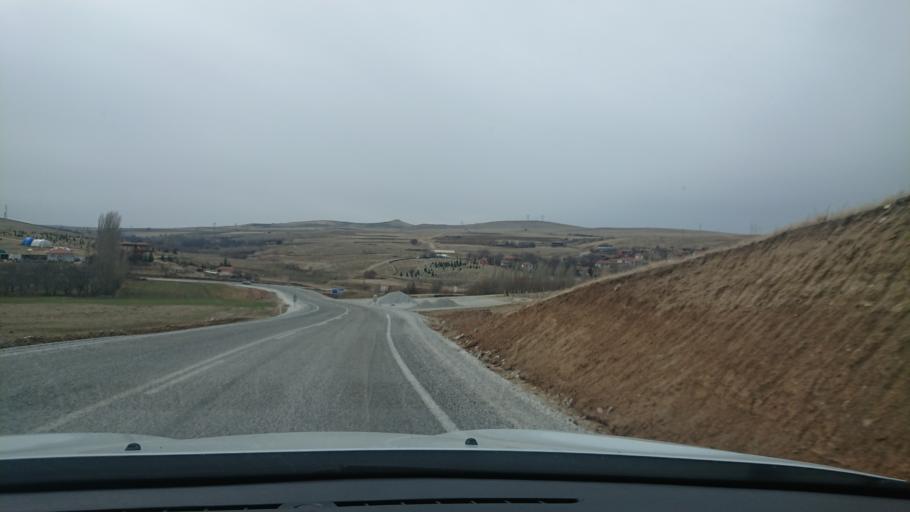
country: TR
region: Aksaray
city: Agacoren
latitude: 38.9198
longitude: 33.9315
